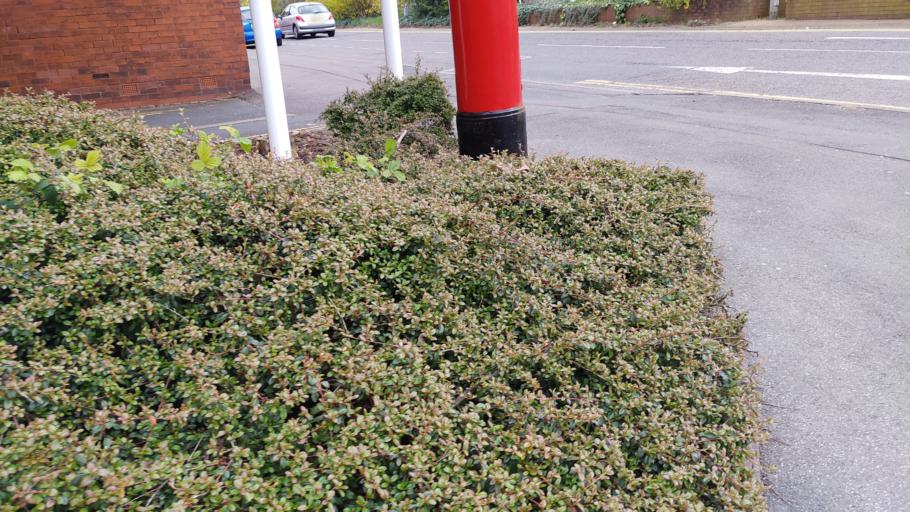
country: GB
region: England
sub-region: Lancashire
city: Preston
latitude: 53.7592
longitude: -2.7174
